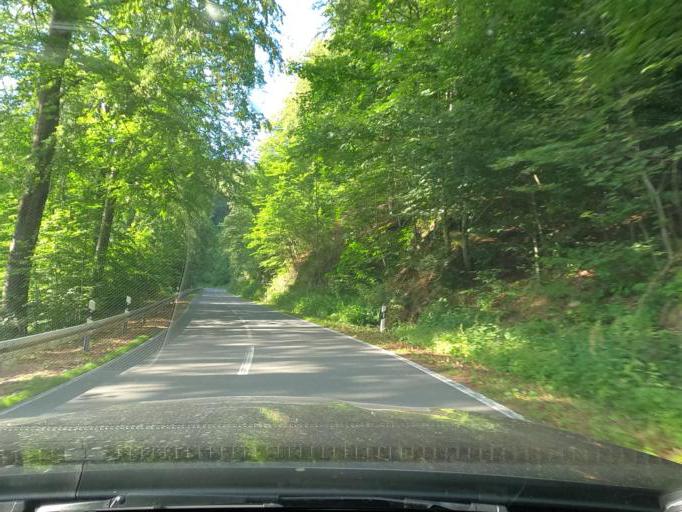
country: DE
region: Lower Saxony
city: Clausthal-Zellerfeld
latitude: 51.7627
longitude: 10.3121
